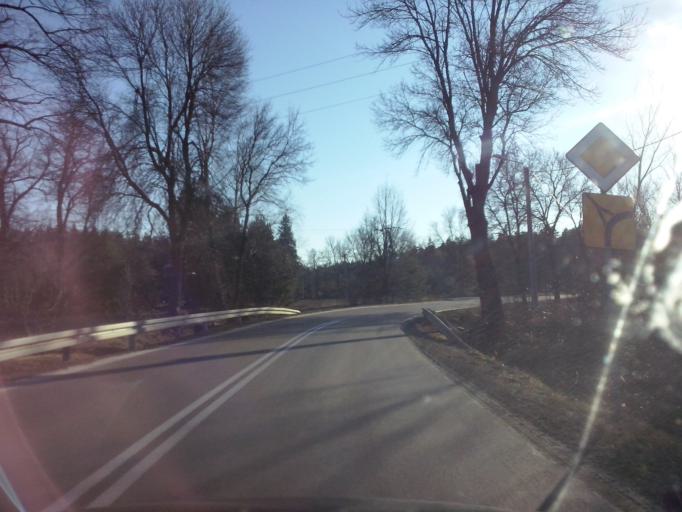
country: PL
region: Subcarpathian Voivodeship
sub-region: Powiat nizanski
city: Harasiuki
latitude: 50.4745
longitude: 22.4727
